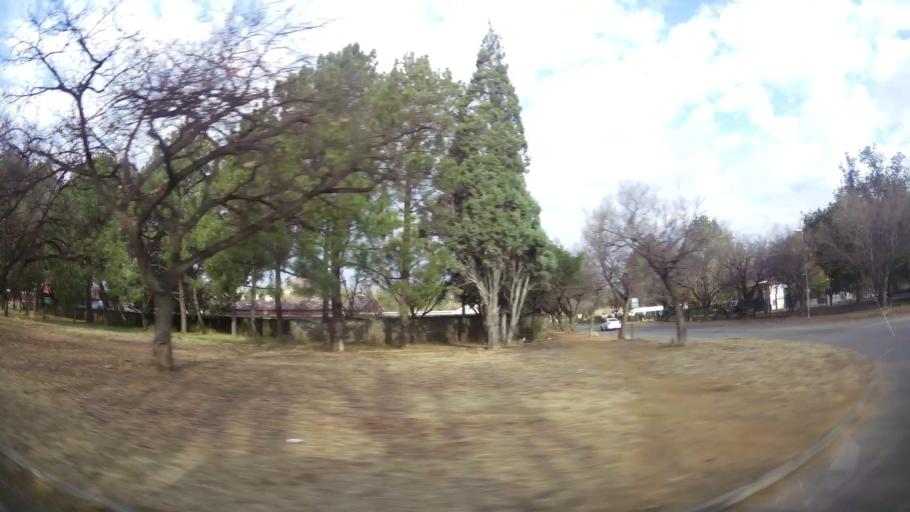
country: ZA
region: Orange Free State
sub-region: Fezile Dabi District Municipality
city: Sasolburg
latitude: -26.8257
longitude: 27.8290
